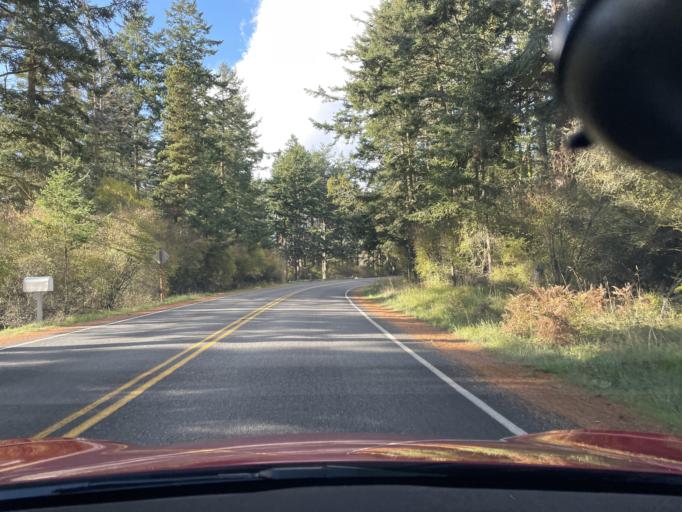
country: US
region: Washington
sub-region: San Juan County
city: Friday Harbor
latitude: 48.4658
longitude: -123.0295
